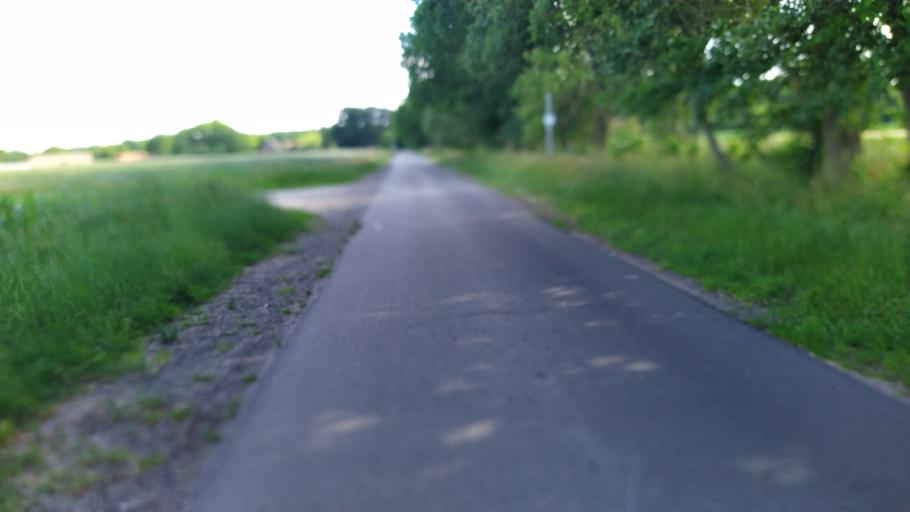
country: DE
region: Lower Saxony
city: Lintig
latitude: 53.6321
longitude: 8.8963
